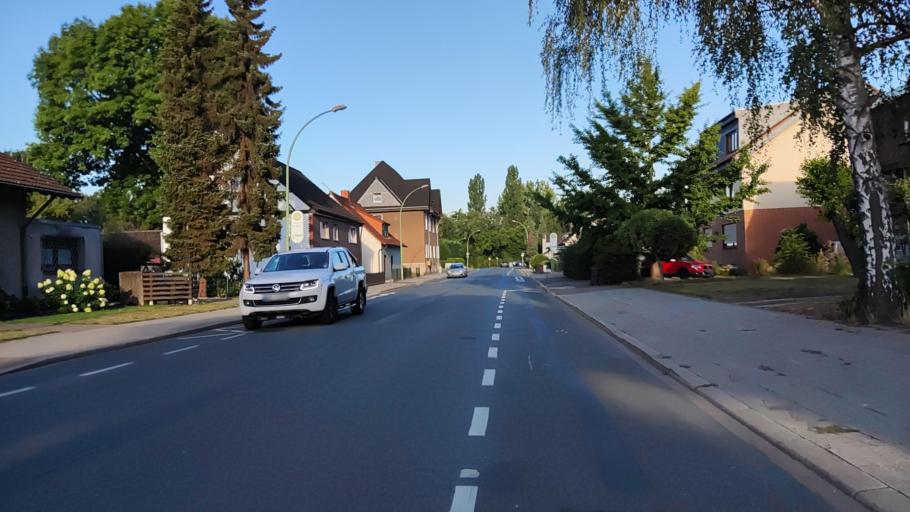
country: DE
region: North Rhine-Westphalia
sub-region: Regierungsbezirk Arnsberg
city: Herne
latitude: 51.5500
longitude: 7.2474
